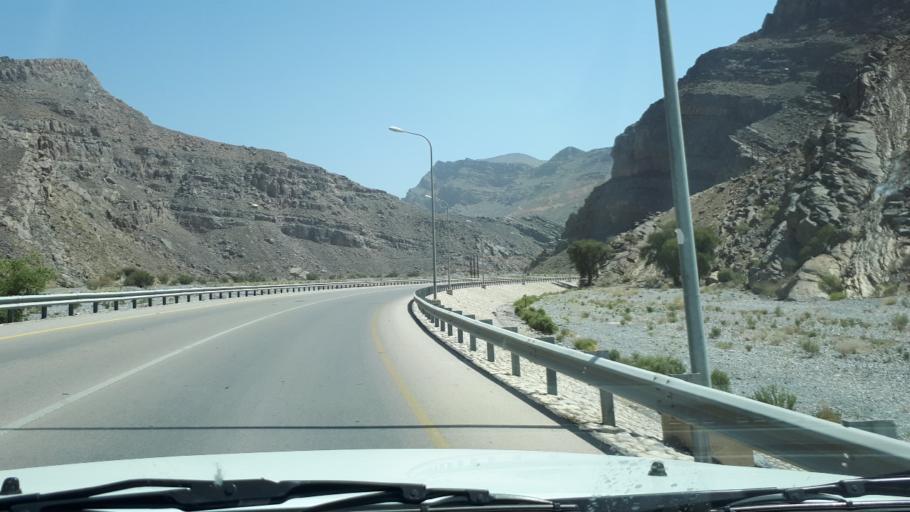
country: OM
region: Muhafazat ad Dakhiliyah
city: Izki
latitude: 22.9284
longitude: 57.6656
